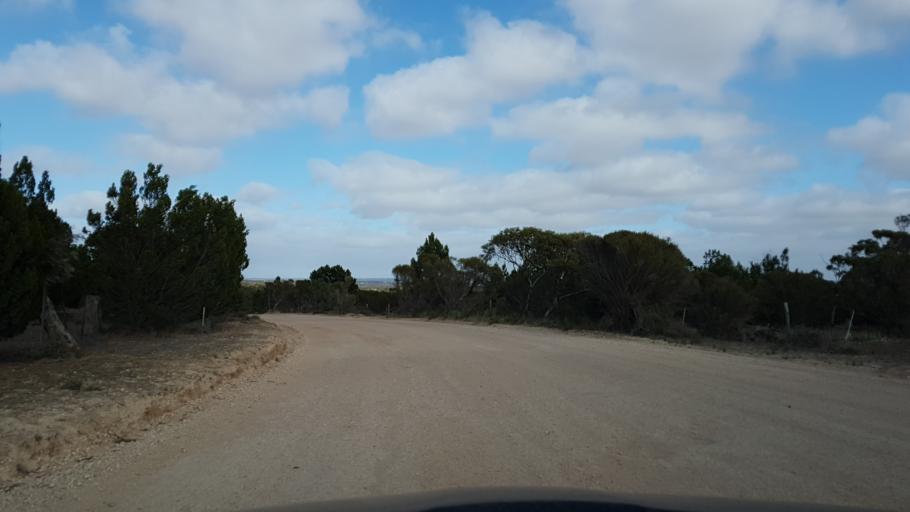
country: AU
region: South Australia
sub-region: Murray Bridge
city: Murray Bridge
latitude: -35.1115
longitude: 139.2063
